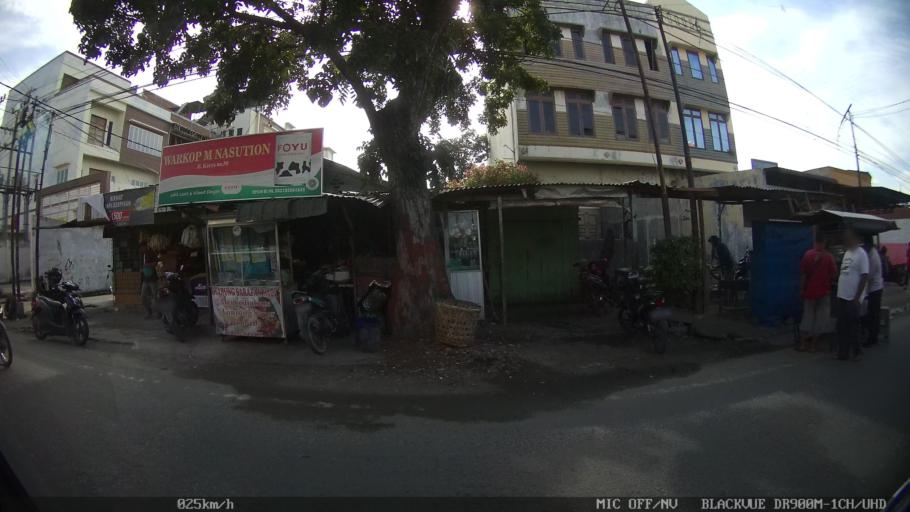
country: ID
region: North Sumatra
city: Medan
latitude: 3.6047
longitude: 98.6650
